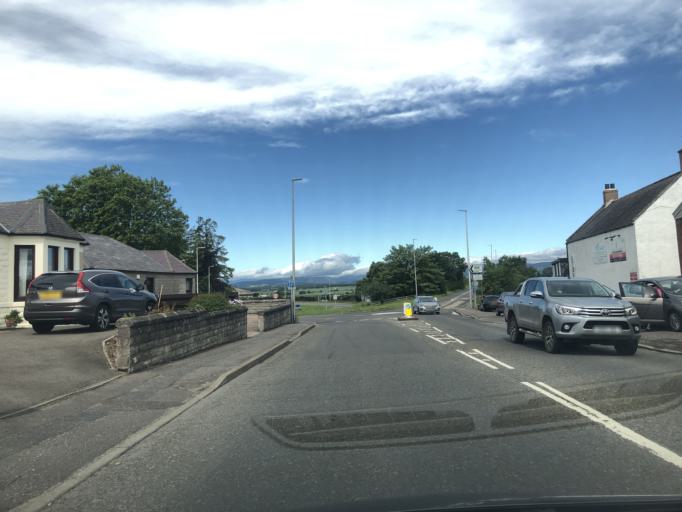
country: GB
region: Scotland
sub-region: Angus
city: Forfar
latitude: 56.6521
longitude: -2.8908
